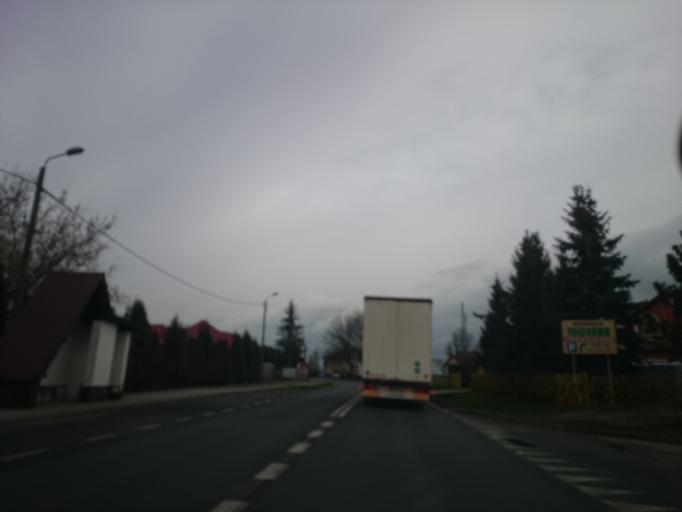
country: PL
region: Opole Voivodeship
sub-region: Powiat nyski
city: Otmuchow
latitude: 50.4451
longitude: 17.1126
